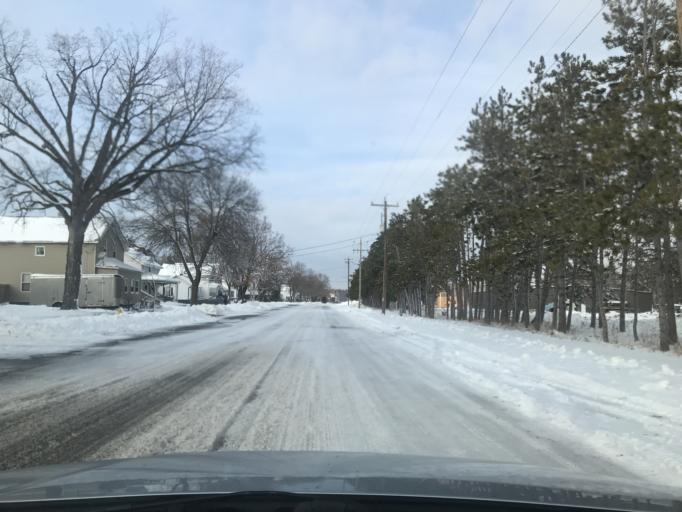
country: US
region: Wisconsin
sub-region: Marinette County
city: Peshtigo
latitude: 45.0497
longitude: -87.7489
